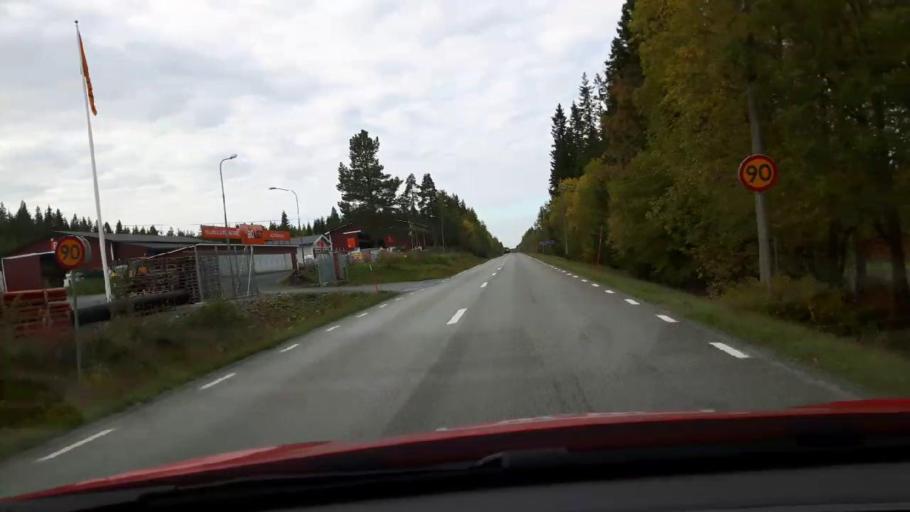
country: SE
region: Jaemtland
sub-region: Krokoms Kommun
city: Krokom
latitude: 63.1878
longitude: 14.0664
